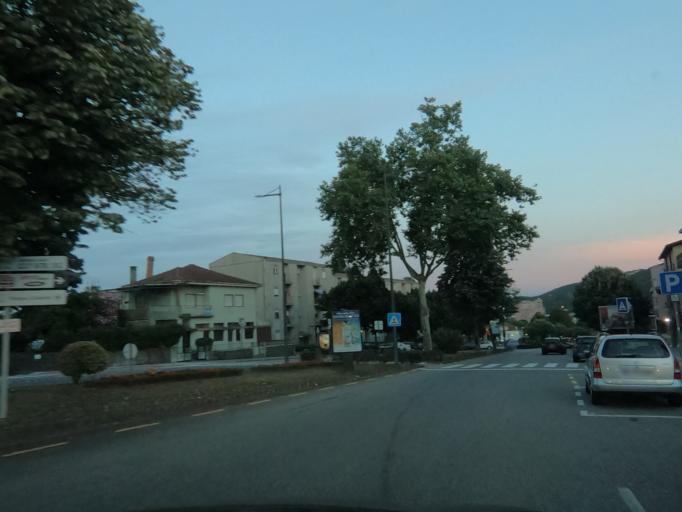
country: PT
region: Porto
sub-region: Valongo
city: Valongo
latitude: 41.1934
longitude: -8.4998
